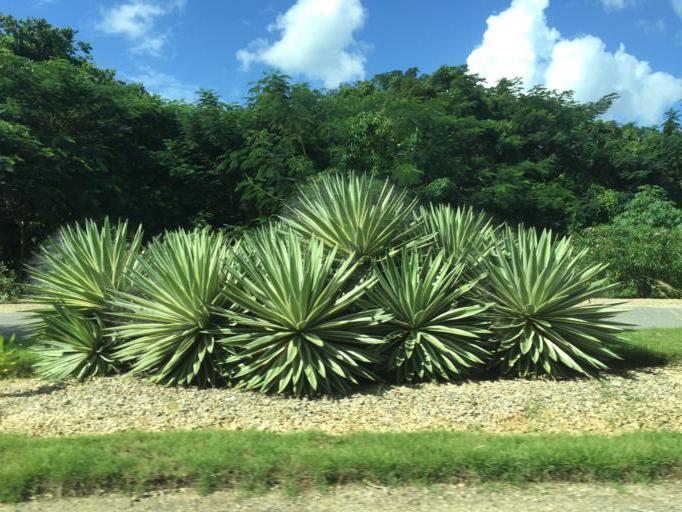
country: DO
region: Santo Domingo
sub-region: Santo Domingo
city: Boca Chica
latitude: 18.4659
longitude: -69.6540
